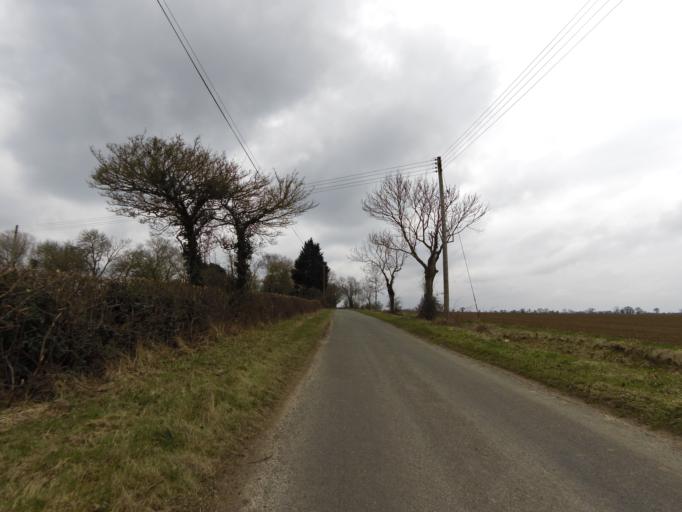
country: GB
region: England
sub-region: Suffolk
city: Halesworth
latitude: 52.3925
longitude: 1.5187
